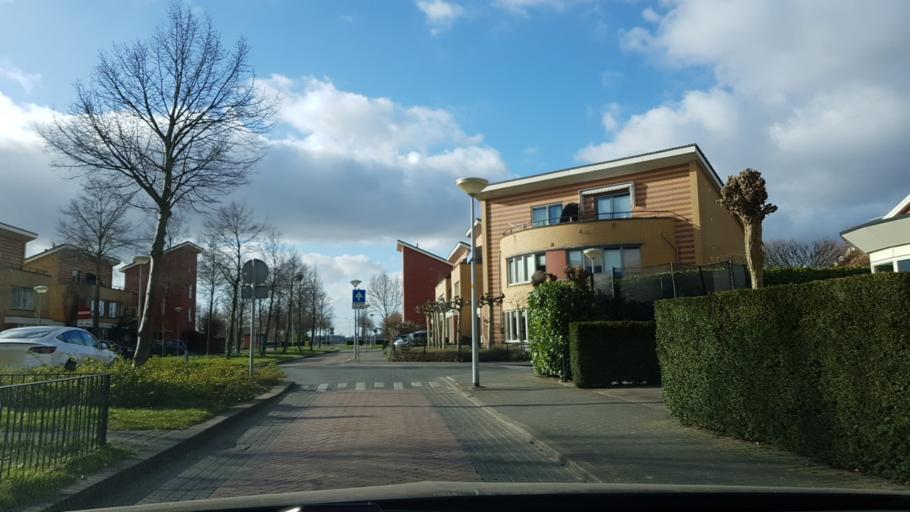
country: NL
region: South Holland
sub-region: Gemeente Hillegom
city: Hillegom
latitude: 52.2712
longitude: 4.6087
